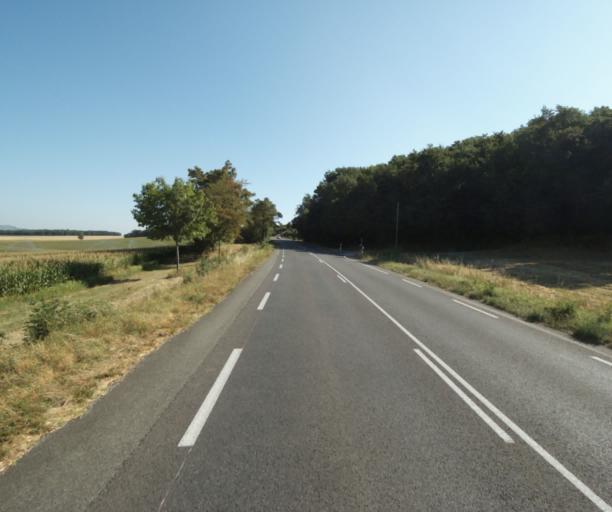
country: FR
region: Midi-Pyrenees
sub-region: Departement du Tarn
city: Soreze
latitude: 43.4941
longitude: 2.0417
